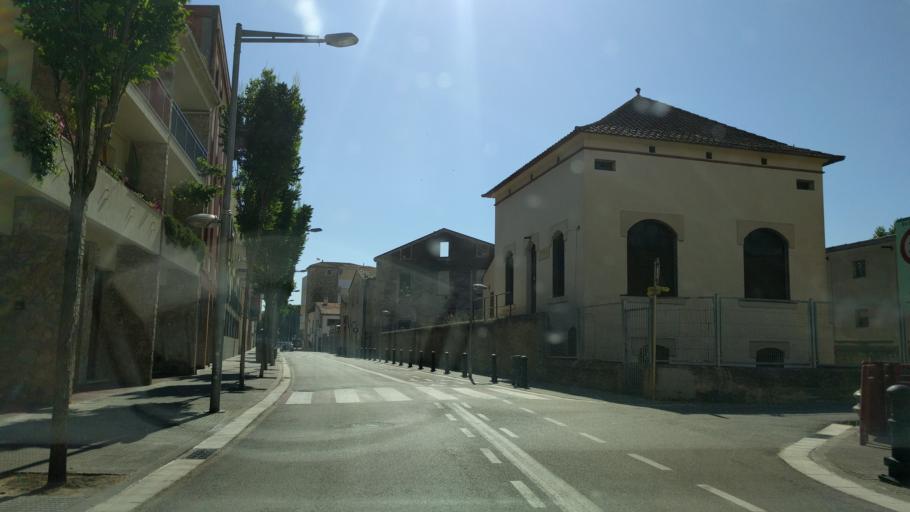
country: ES
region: Catalonia
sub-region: Provincia de Girona
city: Salt
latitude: 41.9769
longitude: 2.7929
